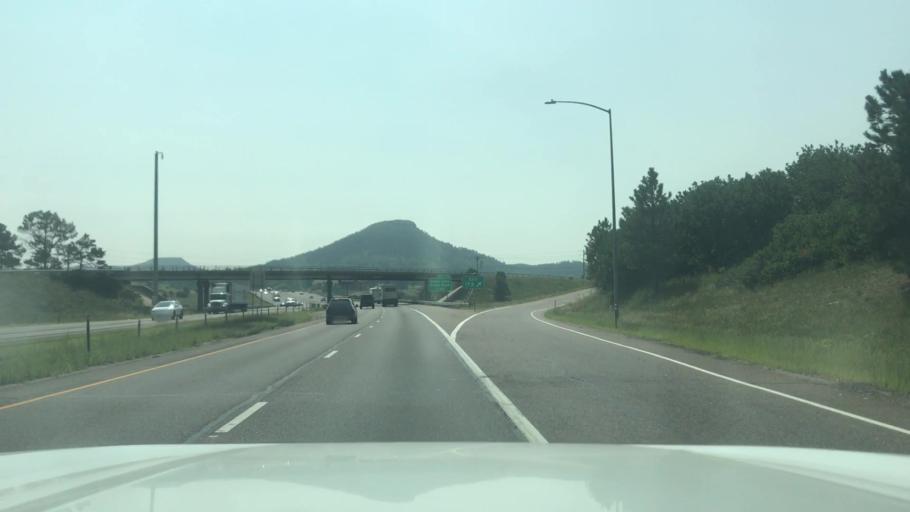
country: US
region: Colorado
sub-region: Douglas County
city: Perry Park
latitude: 39.2498
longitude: -104.8850
